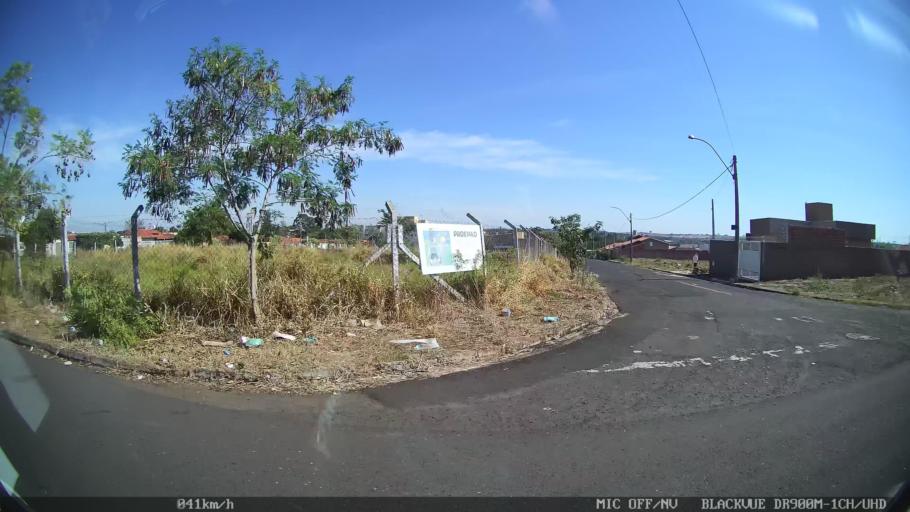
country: BR
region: Sao Paulo
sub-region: Sao Jose Do Rio Preto
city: Sao Jose do Rio Preto
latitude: -20.7690
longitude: -49.4133
